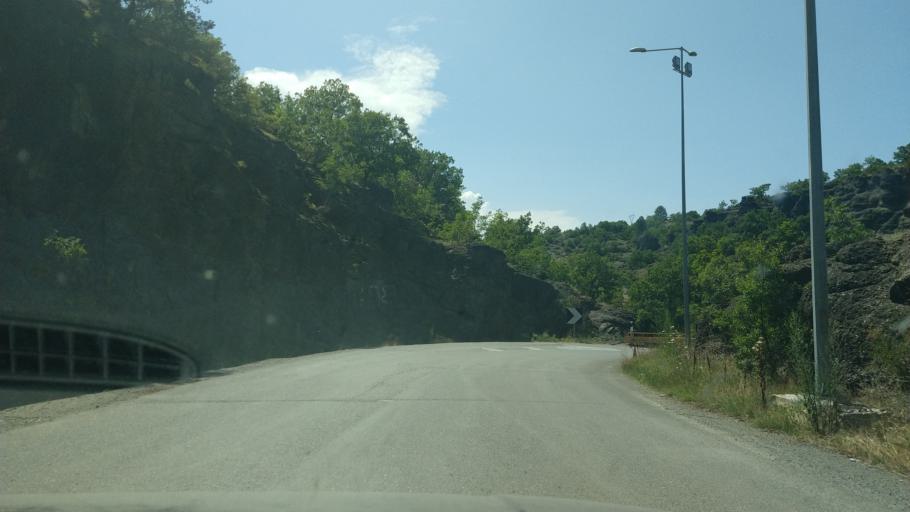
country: GR
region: West Macedonia
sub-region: Nomos Grevenon
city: Grevena
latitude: 40.0510
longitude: 21.4811
